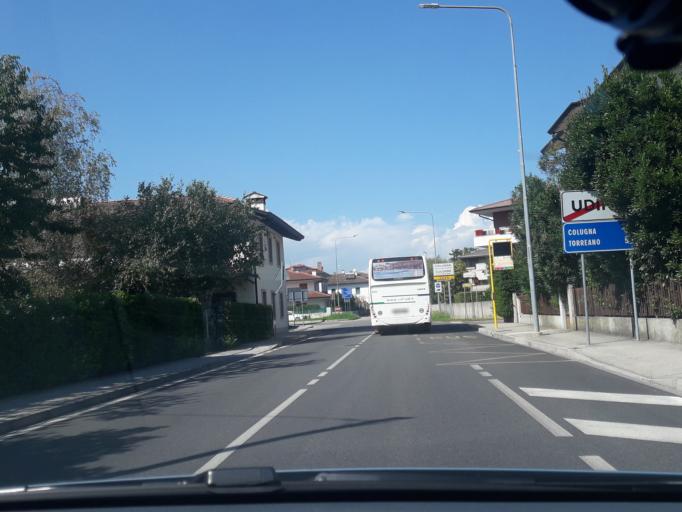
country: IT
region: Friuli Venezia Giulia
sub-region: Provincia di Udine
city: Colugna
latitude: 46.0877
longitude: 13.2015
